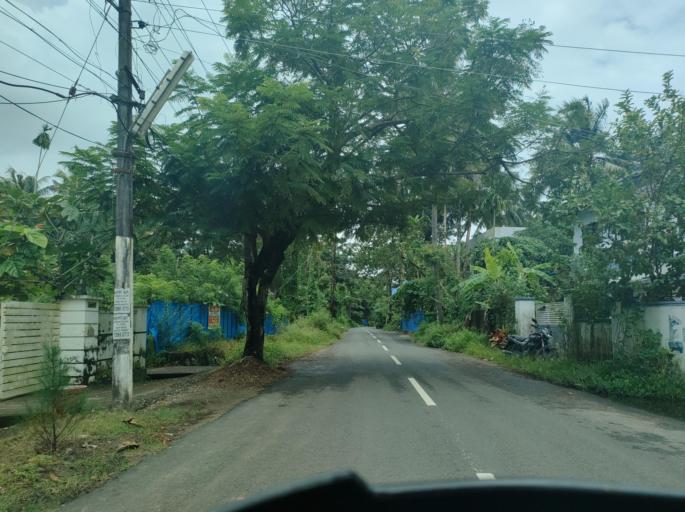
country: IN
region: Kerala
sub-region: Ernakulam
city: Elur
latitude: 10.0560
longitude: 76.2117
